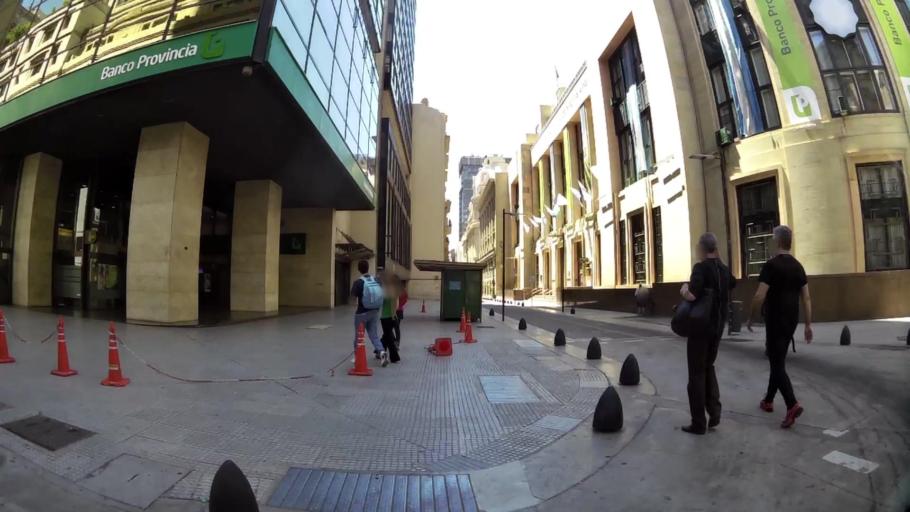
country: AR
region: Buenos Aires F.D.
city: Buenos Aires
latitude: -34.6067
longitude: -58.3739
